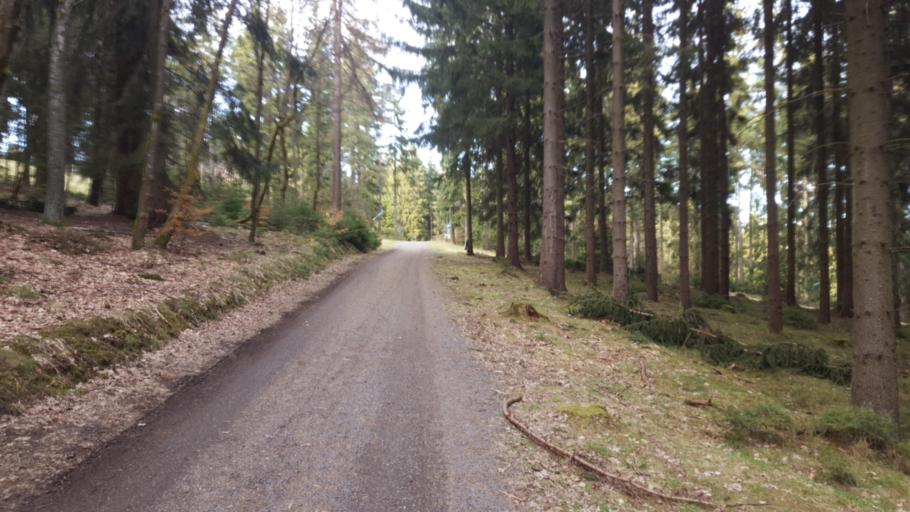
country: CZ
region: Karlovarsky
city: As
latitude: 50.2338
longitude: 12.2070
